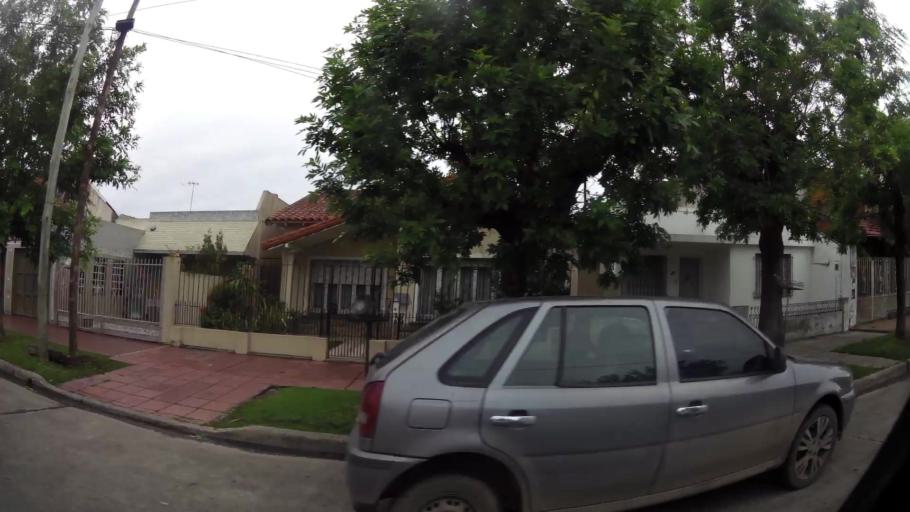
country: AR
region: Buenos Aires
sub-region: Partido de Lanus
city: Lanus
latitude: -34.6988
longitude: -58.3746
